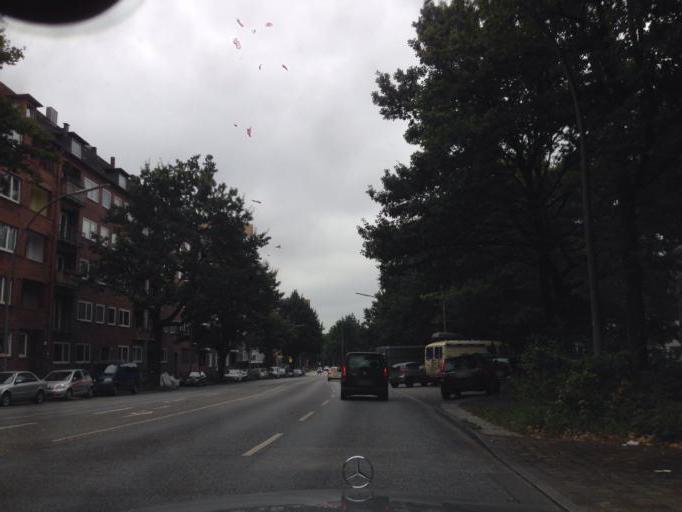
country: DE
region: Hamburg
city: St. Pauli
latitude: 53.5641
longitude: 9.9501
